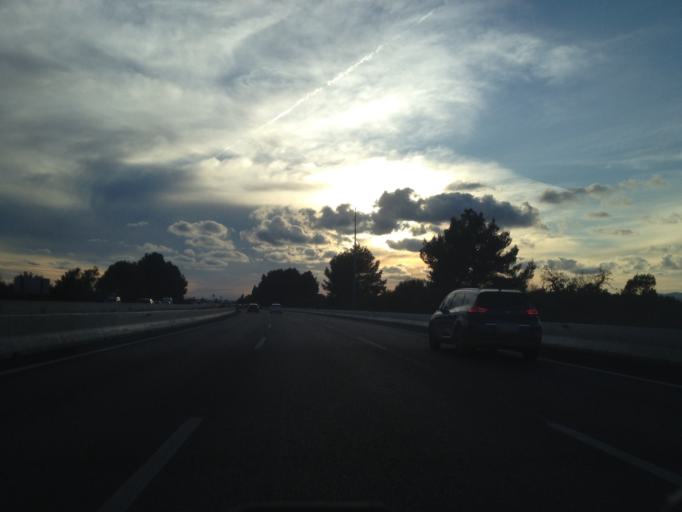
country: ES
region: Balearic Islands
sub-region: Illes Balears
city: Marratxi
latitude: 39.6277
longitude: 2.7169
